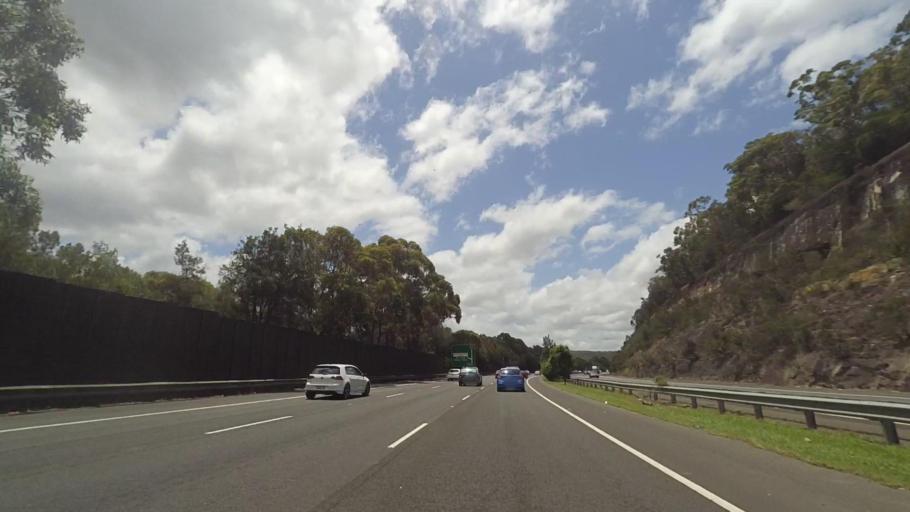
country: AU
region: New South Wales
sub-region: Ku-ring-gai
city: North Wahroonga
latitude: -33.7007
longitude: 151.1181
